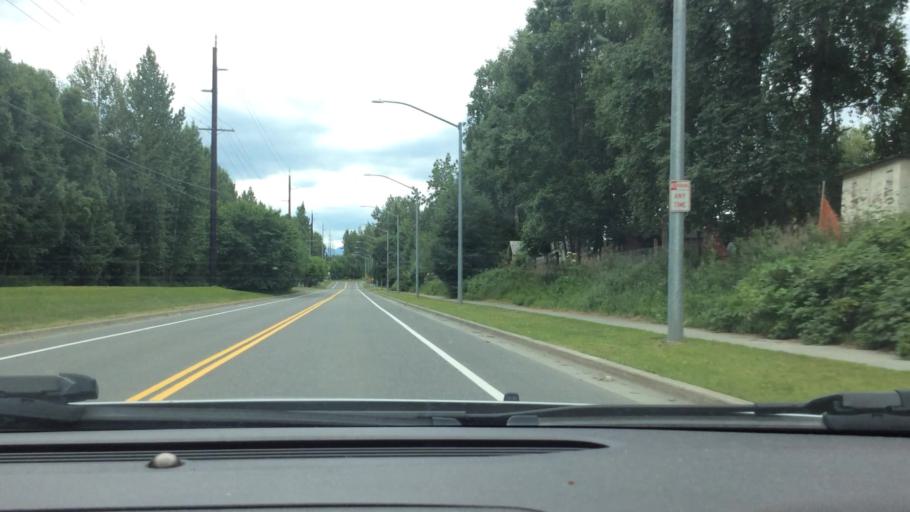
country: US
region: Alaska
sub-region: Anchorage Municipality
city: Anchorage
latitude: 61.2075
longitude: -149.7933
